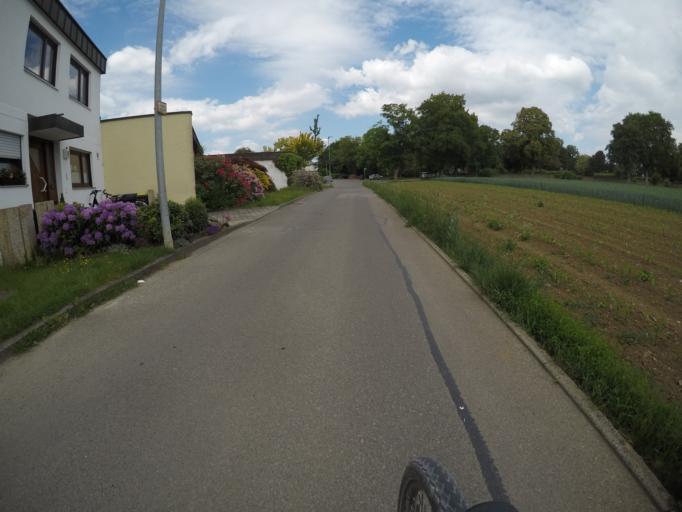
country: DE
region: Baden-Wuerttemberg
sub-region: Regierungsbezirk Stuttgart
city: Kongen
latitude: 48.6910
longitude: 9.3694
